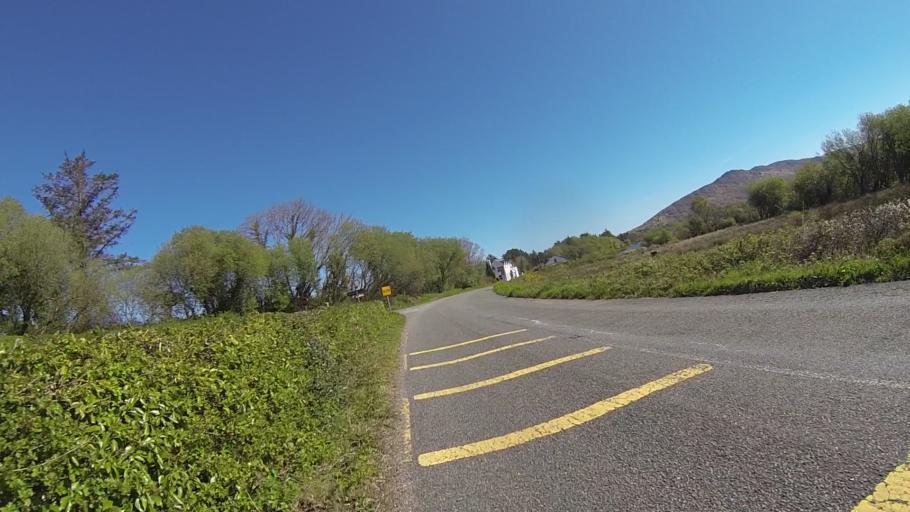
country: IE
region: Munster
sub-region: Ciarrai
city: Kenmare
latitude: 51.8175
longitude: -9.7412
